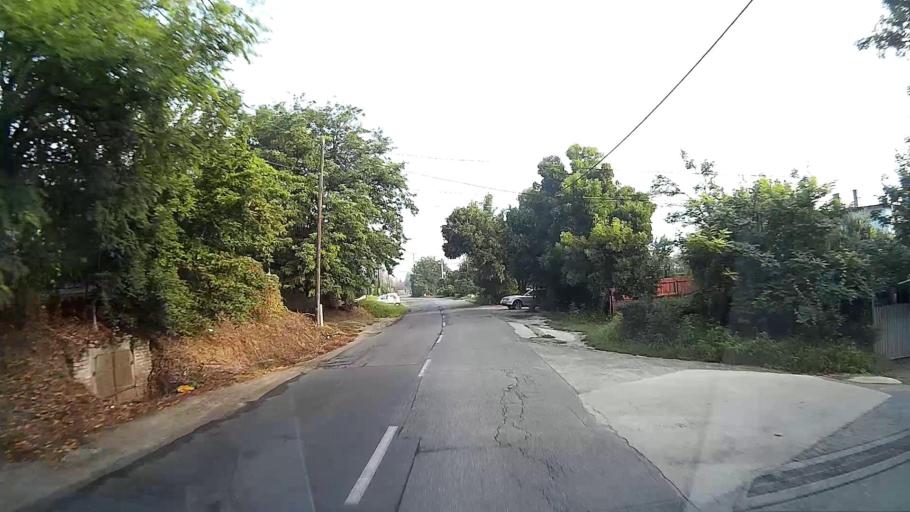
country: HU
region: Pest
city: Tahitotfalu
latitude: 47.7477
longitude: 19.0961
